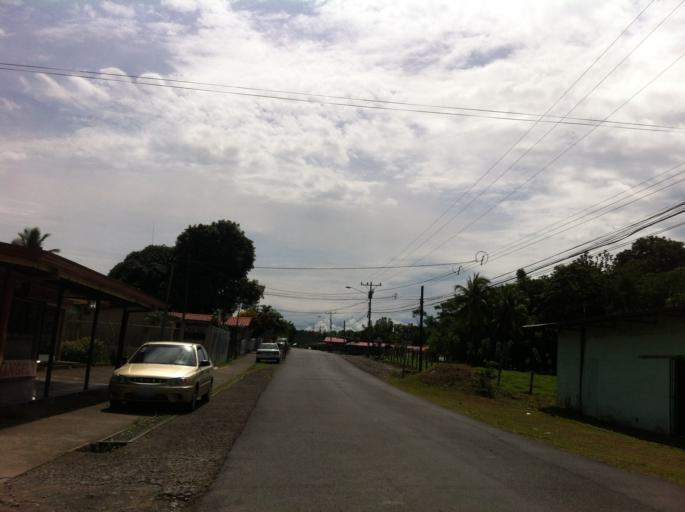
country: CR
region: San Jose
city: Dulce Nombre de Jesus
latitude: 10.3385
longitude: -83.9561
